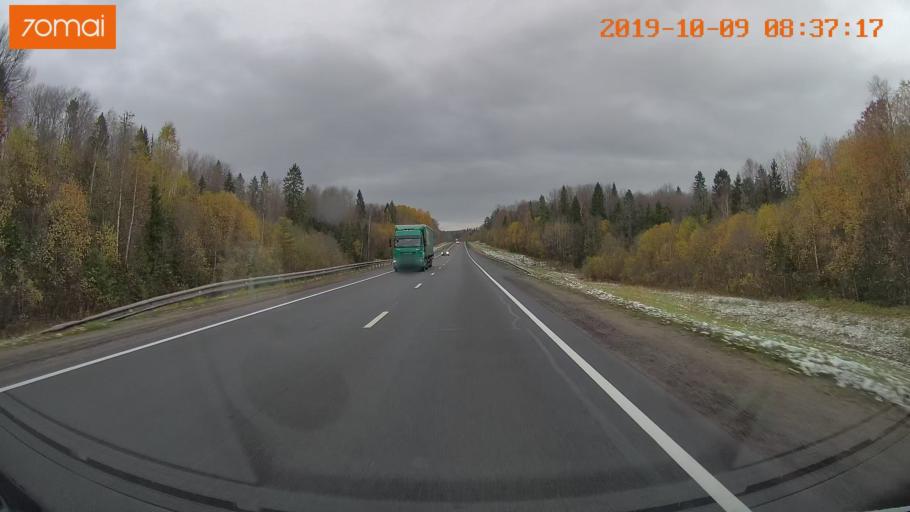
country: RU
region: Vologda
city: Gryazovets
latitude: 58.9391
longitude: 40.1750
